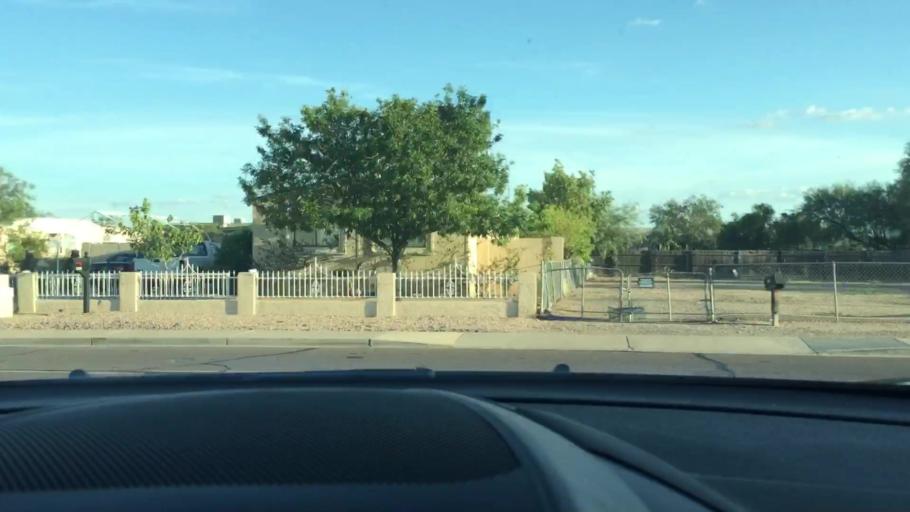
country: US
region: Arizona
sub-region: Maricopa County
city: Surprise
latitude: 33.6367
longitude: -112.3375
